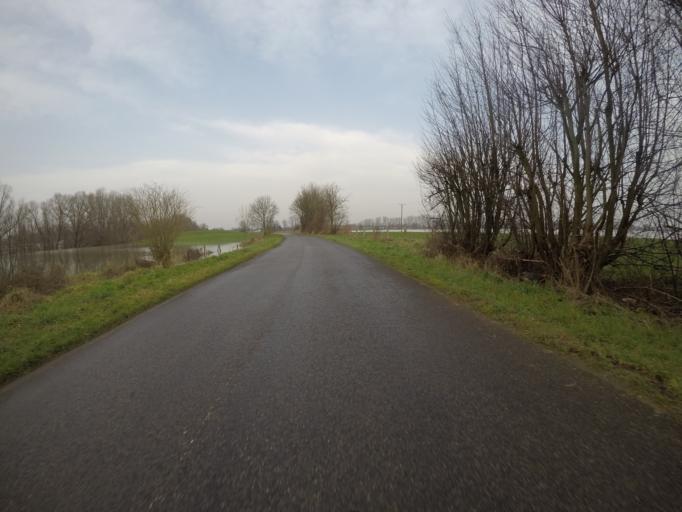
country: DE
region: North Rhine-Westphalia
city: Rees
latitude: 51.7479
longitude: 6.3988
